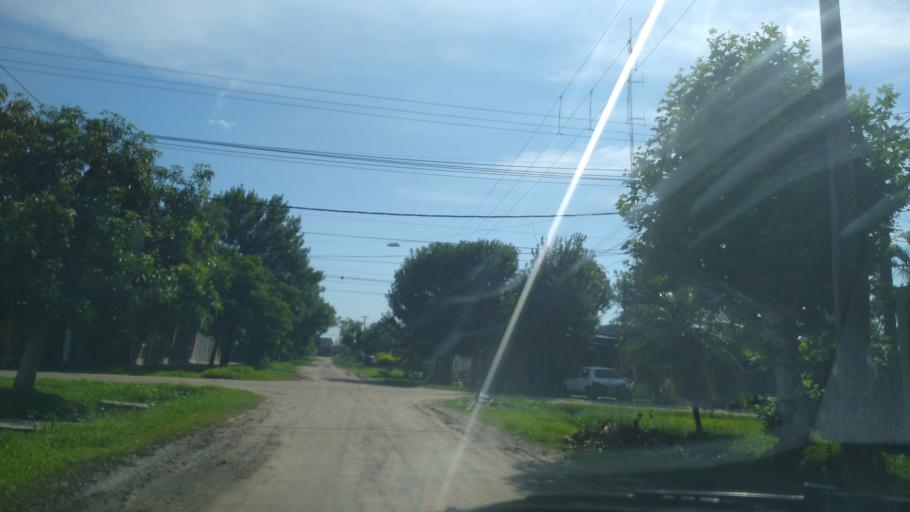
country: AR
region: Chaco
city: Barranqueras
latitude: -27.4886
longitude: -58.9547
